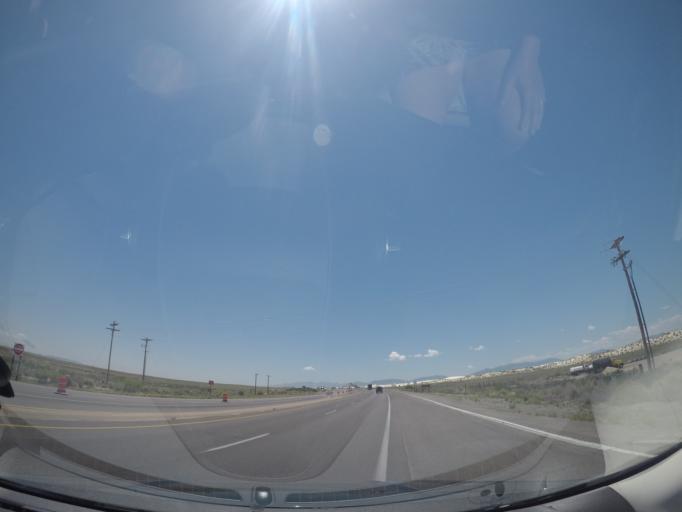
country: US
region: New Mexico
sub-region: Otero County
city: Holloman Air Force Base
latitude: 32.7786
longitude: -106.1726
